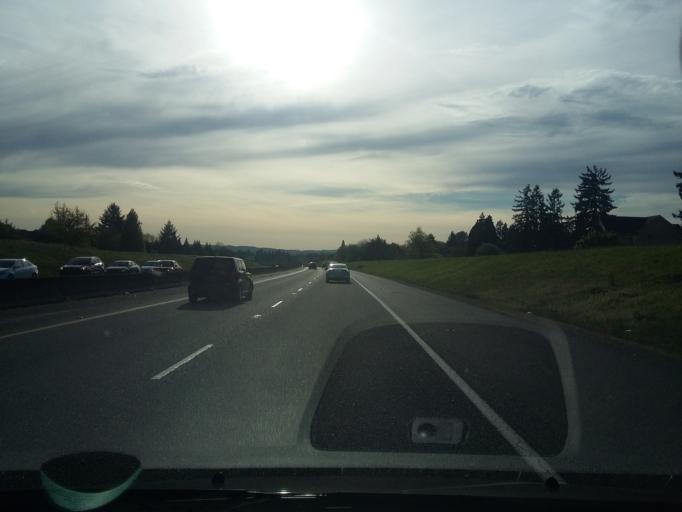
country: US
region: Washington
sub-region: Clark County
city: Walnut Grove
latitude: 45.6480
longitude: -122.6190
